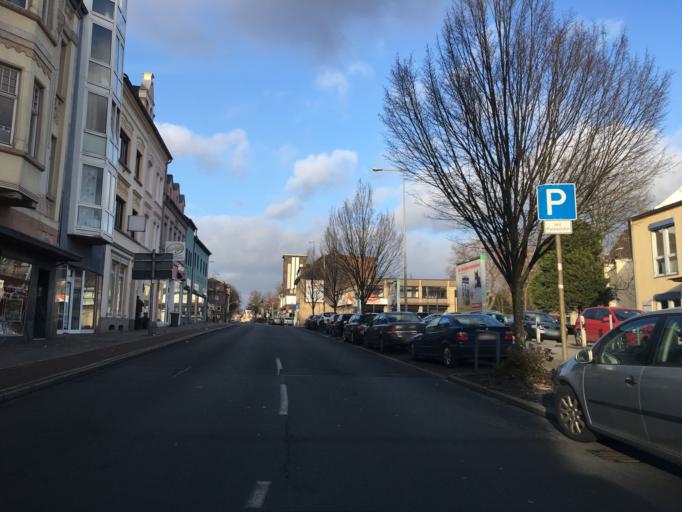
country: DE
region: North Rhine-Westphalia
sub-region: Regierungsbezirk Dusseldorf
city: Oberhausen
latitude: 51.5174
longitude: 6.8467
